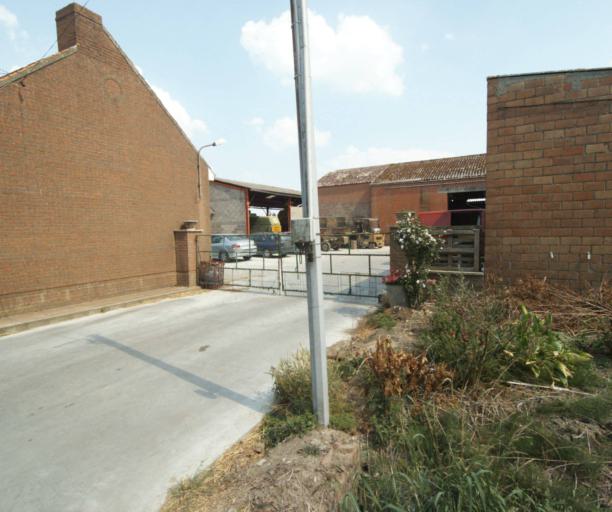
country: FR
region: Nord-Pas-de-Calais
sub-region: Departement du Nord
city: Comines
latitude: 50.7367
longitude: 3.0278
